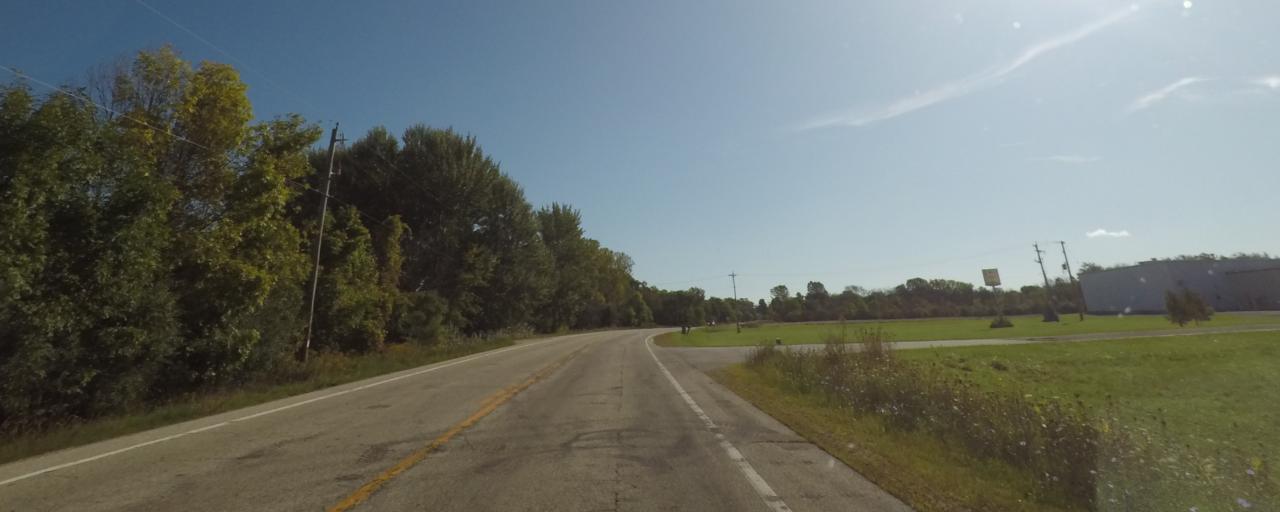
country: US
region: Wisconsin
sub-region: Waukesha County
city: Dousman
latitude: 43.0130
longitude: -88.5982
